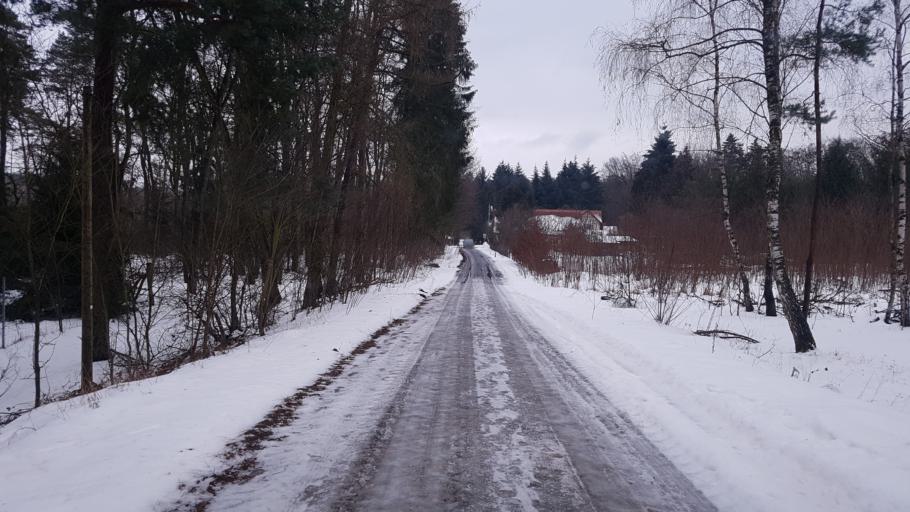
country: DE
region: Brandenburg
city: Bronkow
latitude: 51.6538
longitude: 13.9405
